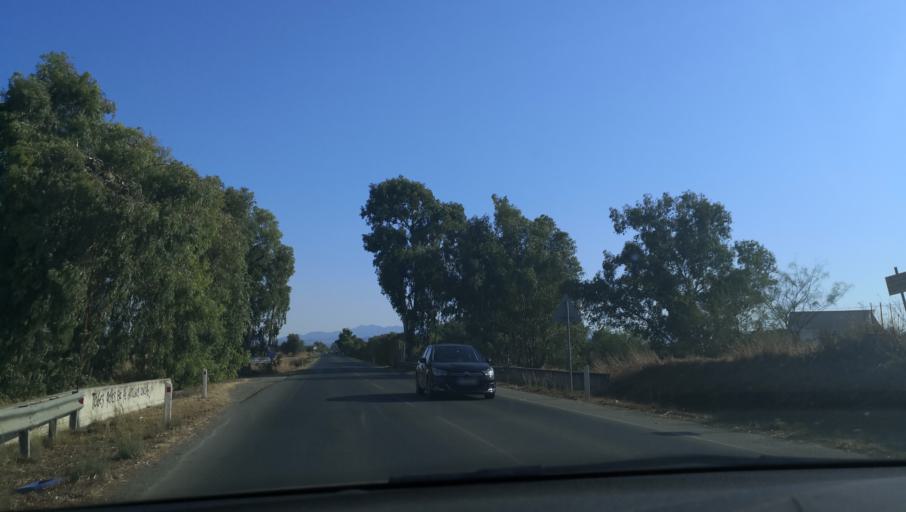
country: CY
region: Lefkosia
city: Pano Deftera
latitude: 35.0718
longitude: 33.2688
